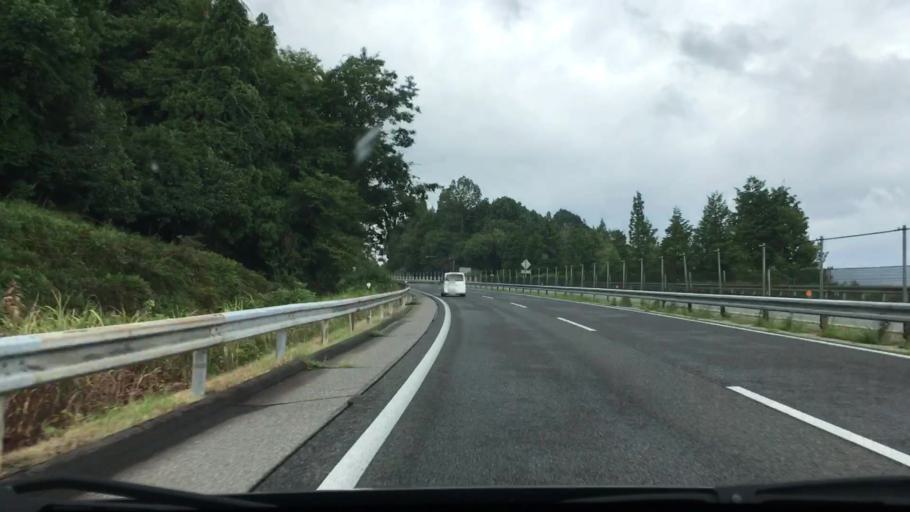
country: JP
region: Hiroshima
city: Miyoshi
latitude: 34.7193
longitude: 132.6522
